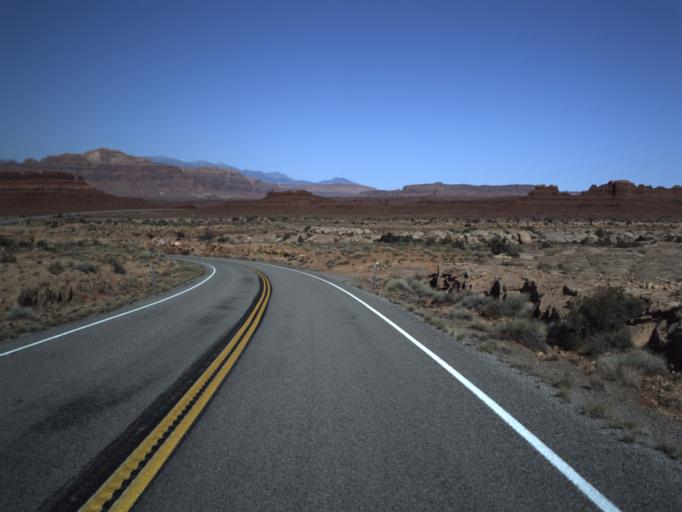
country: US
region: Utah
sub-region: San Juan County
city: Blanding
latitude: 37.8181
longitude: -110.3466
